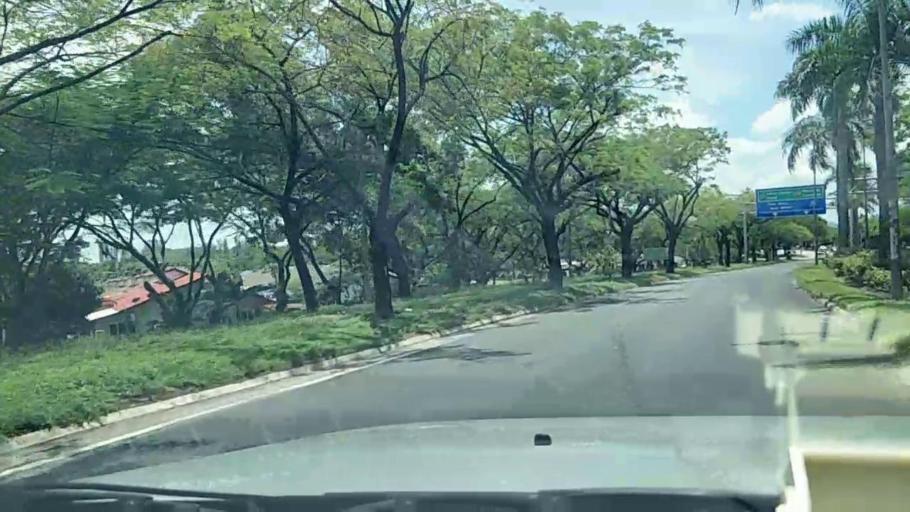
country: MY
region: Putrajaya
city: Putrajaya
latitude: 2.9636
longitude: 101.6167
